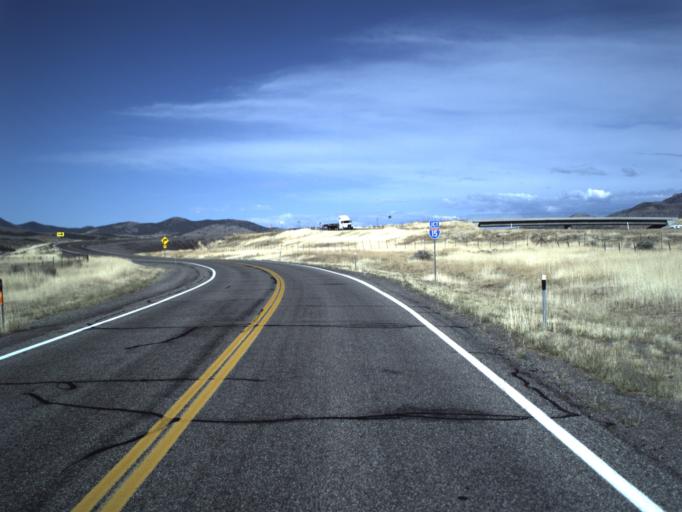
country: US
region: Utah
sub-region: Millard County
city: Fillmore
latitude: 39.1423
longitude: -112.2395
